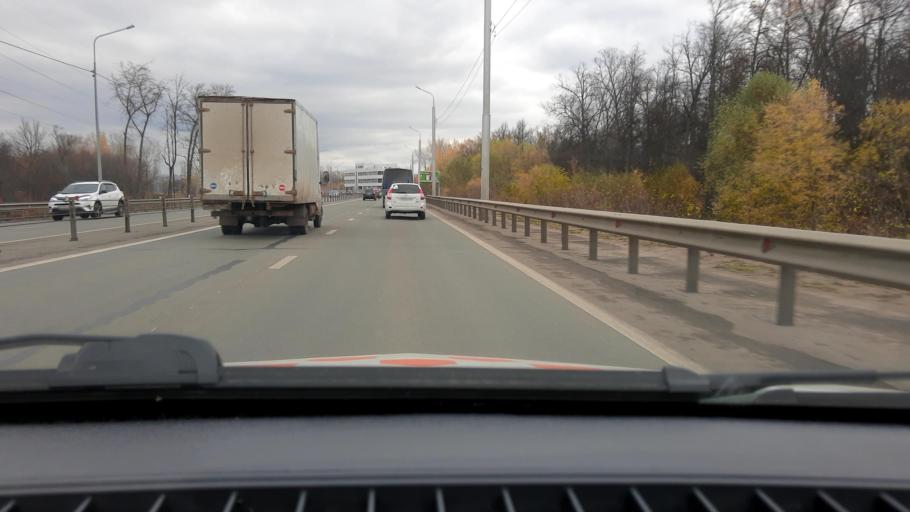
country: RU
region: Bashkortostan
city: Ufa
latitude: 54.6986
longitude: 55.8886
